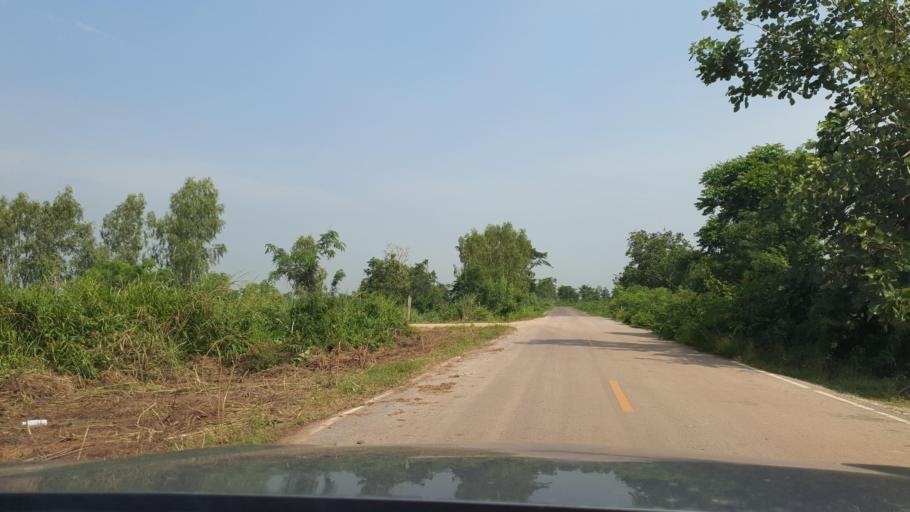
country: TH
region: Phitsanulok
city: Bang Rakam
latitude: 16.8035
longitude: 100.1140
